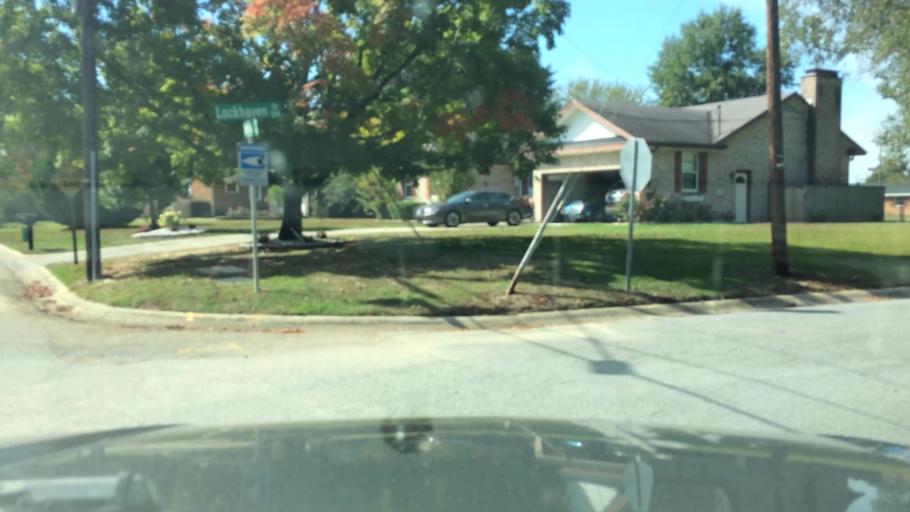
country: US
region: North Carolina
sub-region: Wayne County
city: Goldsboro
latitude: 35.3948
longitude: -77.9598
